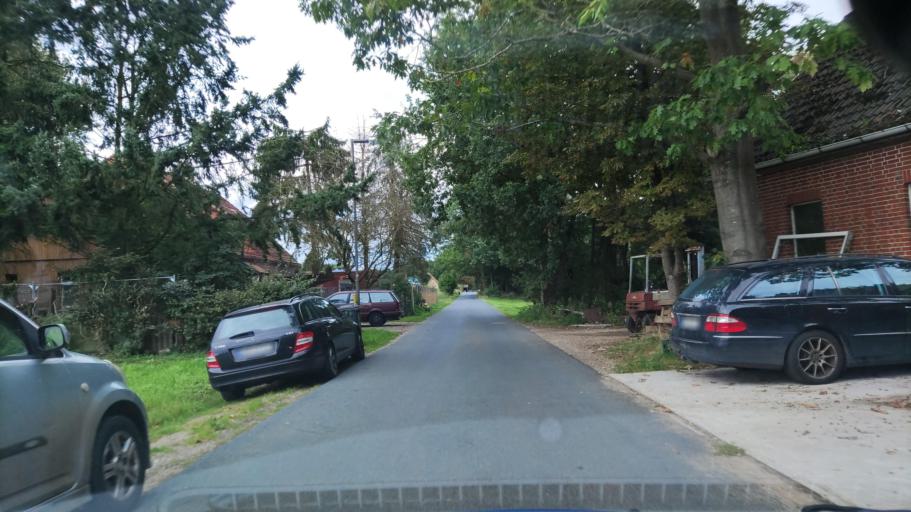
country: DE
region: Lower Saxony
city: Bispingen
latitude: 53.1383
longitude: 10.0221
